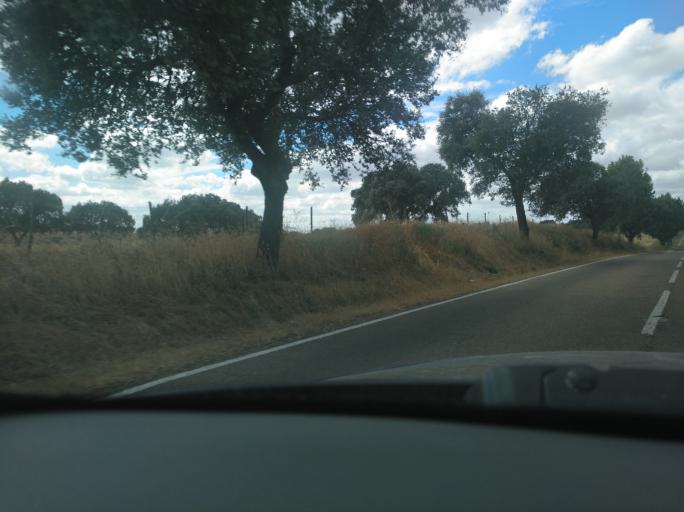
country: PT
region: Portalegre
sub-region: Arronches
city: Arronches
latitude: 39.0430
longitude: -7.4259
